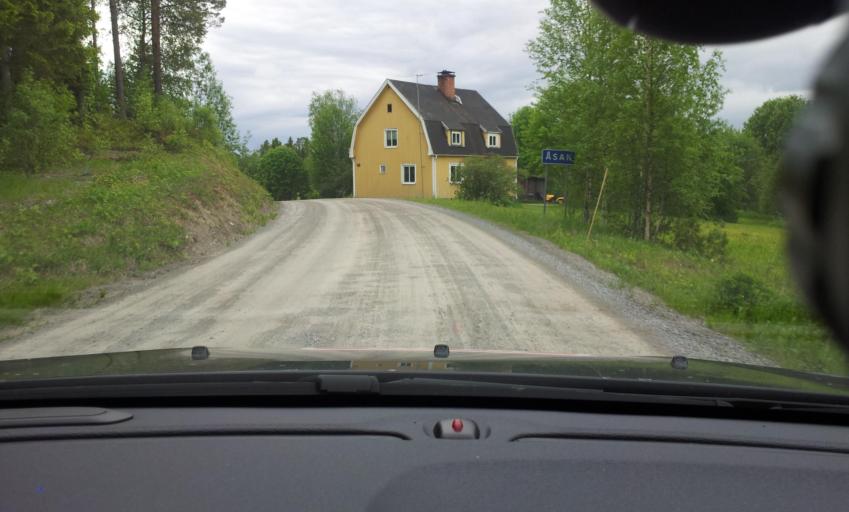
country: SE
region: Jaemtland
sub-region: OEstersunds Kommun
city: Brunflo
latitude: 62.9794
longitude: 14.6945
